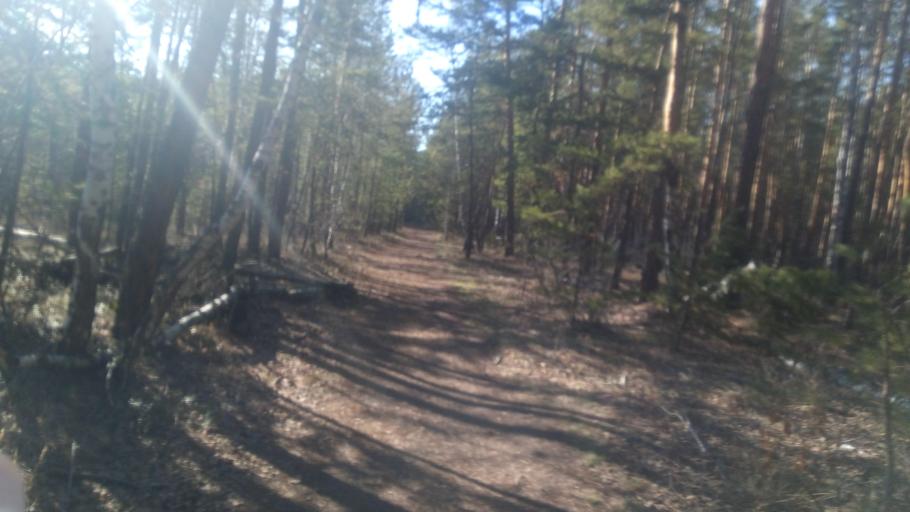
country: RU
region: Chelyabinsk
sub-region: Gorod Chelyabinsk
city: Chelyabinsk
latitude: 55.1602
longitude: 61.3344
